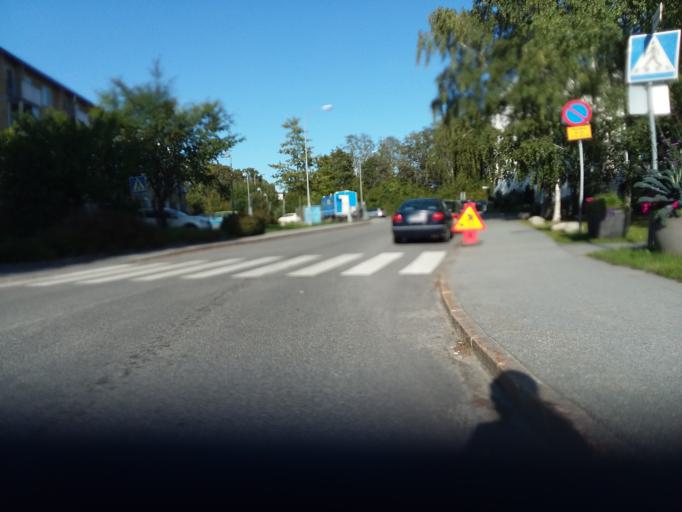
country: SE
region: Stockholm
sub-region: Stockholms Kommun
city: Bromma
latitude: 59.3567
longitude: 17.8721
